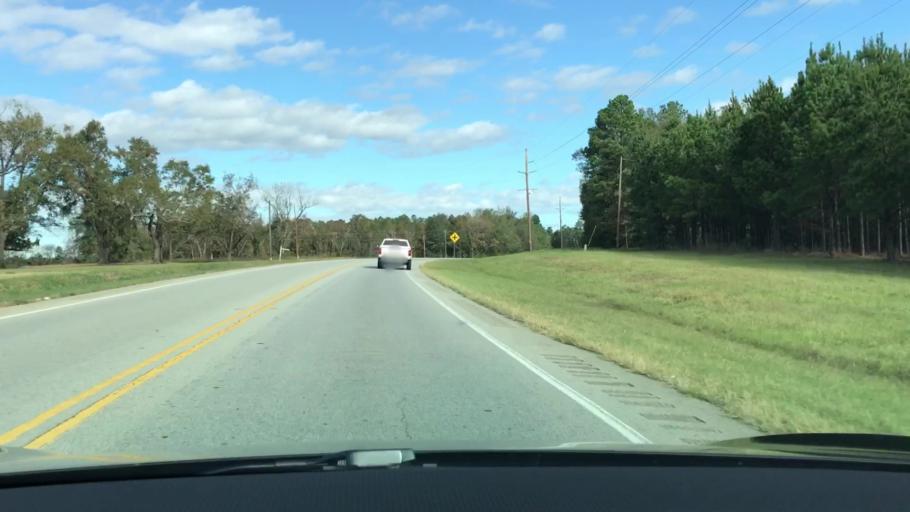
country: US
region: Georgia
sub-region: Jefferson County
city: Louisville
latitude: 33.0505
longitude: -82.4066
